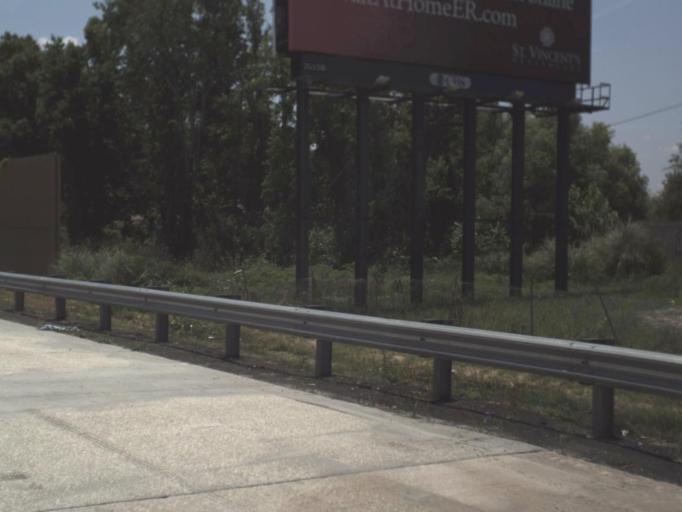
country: US
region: Florida
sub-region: Duval County
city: Jacksonville
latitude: 30.2977
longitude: -81.6375
